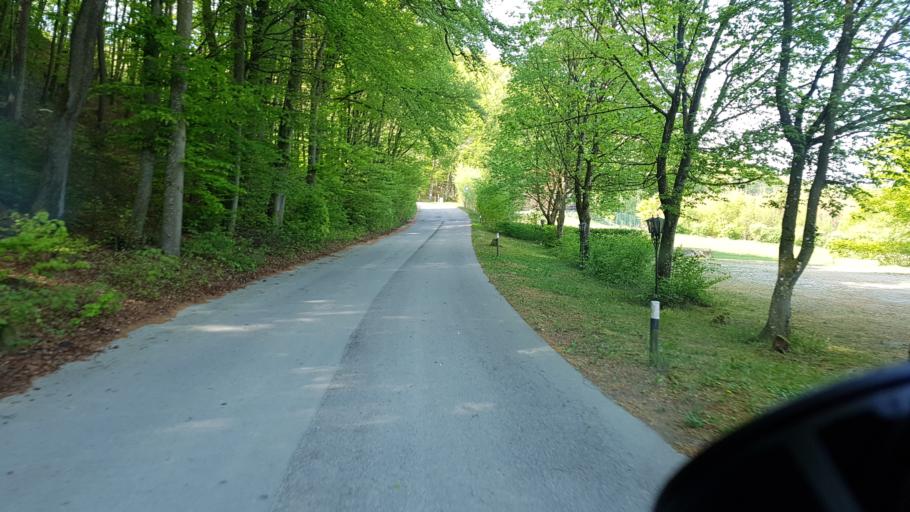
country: DE
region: Bavaria
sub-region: Upper Bavaria
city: Perach
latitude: 48.2394
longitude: 12.7540
